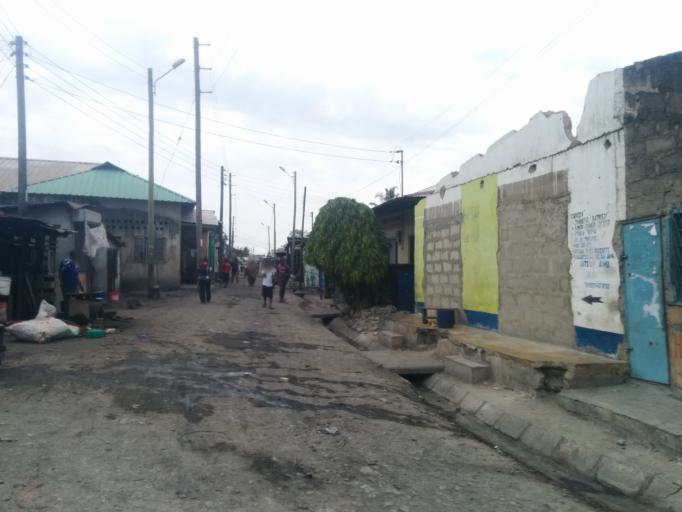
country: TZ
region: Dar es Salaam
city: Dar es Salaam
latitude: -6.8342
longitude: 39.2776
